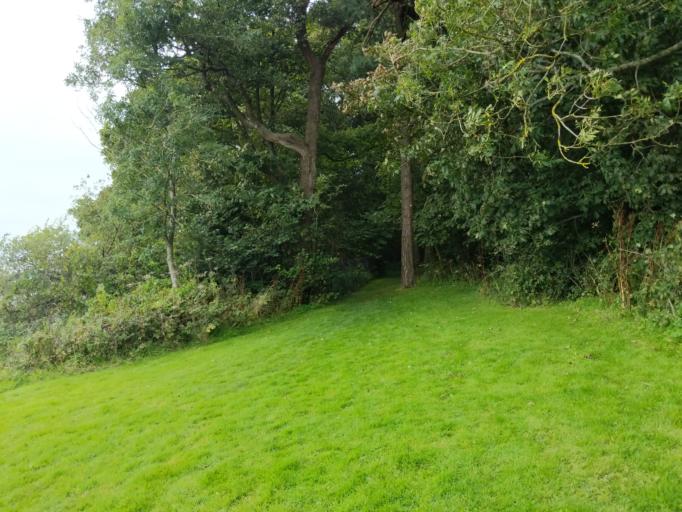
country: GB
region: Scotland
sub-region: Perth and Kinross
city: Kinross
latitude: 56.2010
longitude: -3.3928
